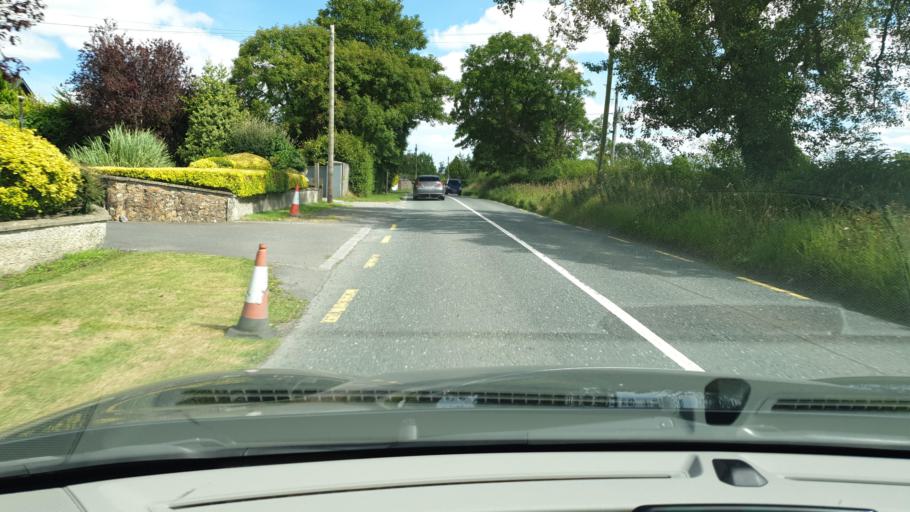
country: IE
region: Leinster
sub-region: Kildare
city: Maynooth
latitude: 53.4396
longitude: -6.5488
